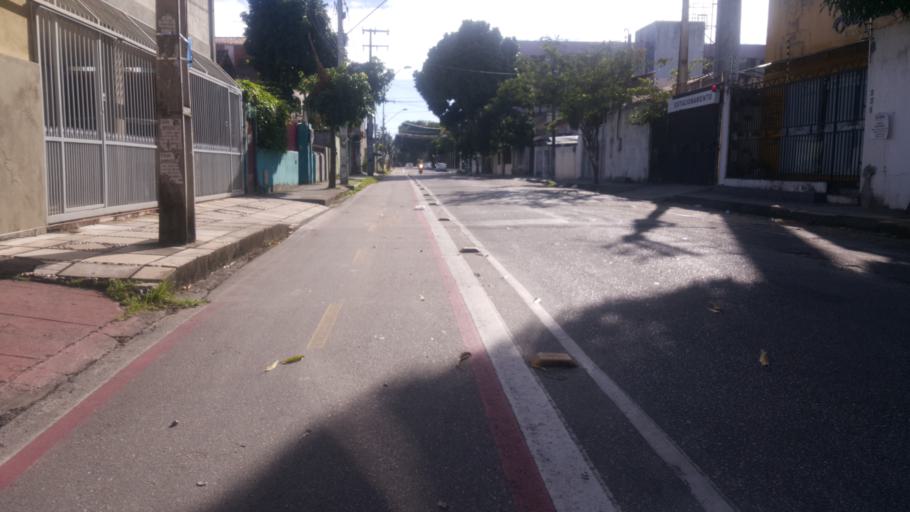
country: BR
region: Ceara
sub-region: Fortaleza
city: Fortaleza
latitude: -3.7443
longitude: -38.5390
